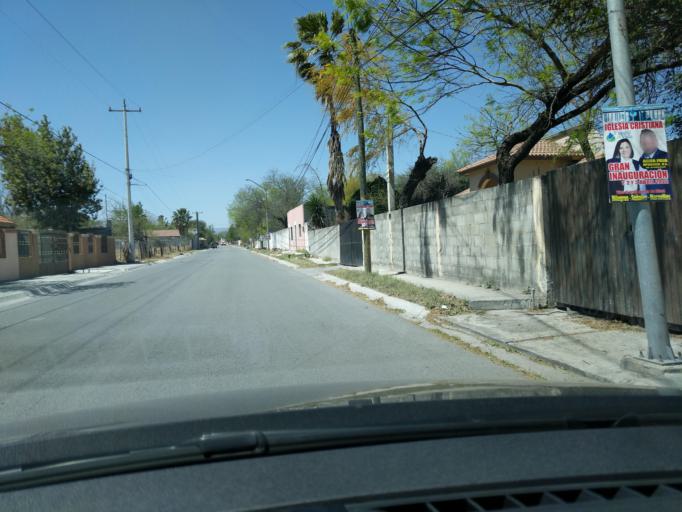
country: MX
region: Nuevo Leon
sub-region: Apodaca
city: Artemio Trevino
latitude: 25.8130
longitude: -100.1406
